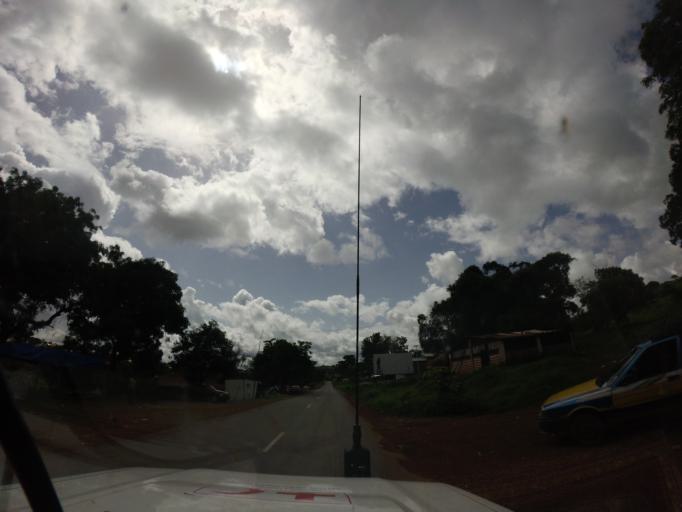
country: GN
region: Mamou
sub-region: Mamou Prefecture
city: Mamou
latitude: 10.3643
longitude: -12.0624
